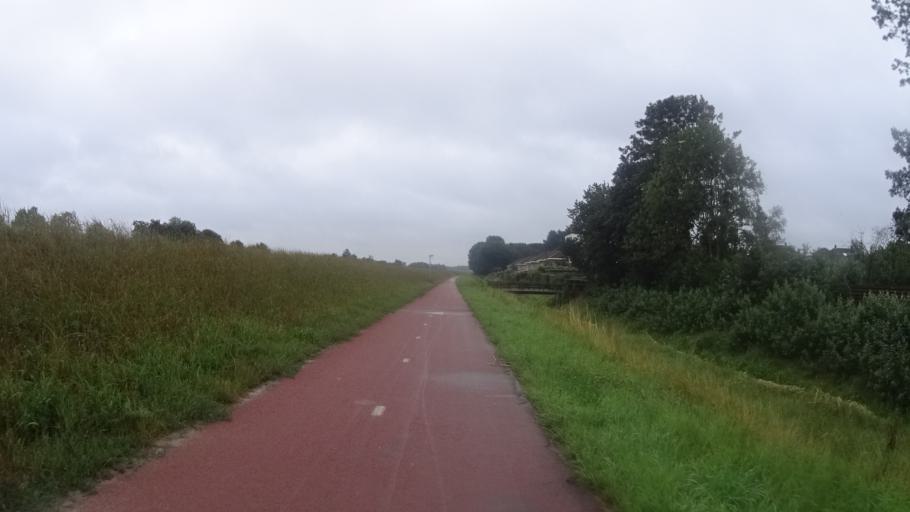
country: NL
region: Groningen
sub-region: Gemeente  Oldambt
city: Winschoten
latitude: 53.1592
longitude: 7.0375
